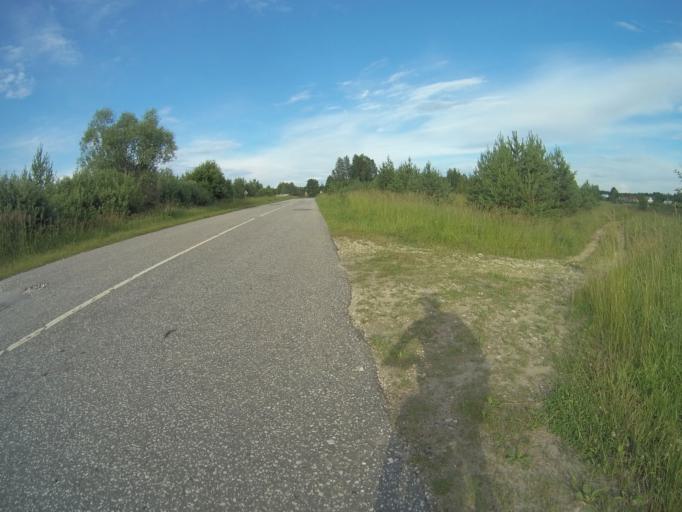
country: RU
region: Vladimir
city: Sudogda
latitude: 56.0647
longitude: 40.8813
